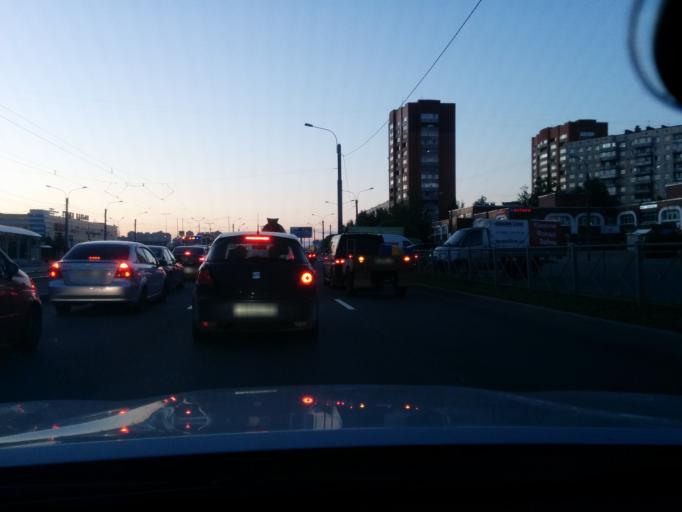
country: RU
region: Leningrad
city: Parnas
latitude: 60.0554
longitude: 30.3370
